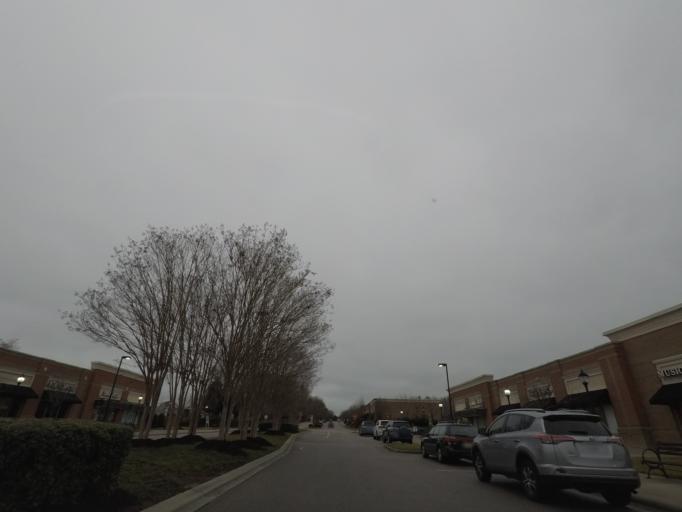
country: US
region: North Carolina
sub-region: Orange County
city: Chapel Hill
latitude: 35.9499
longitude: -78.9896
